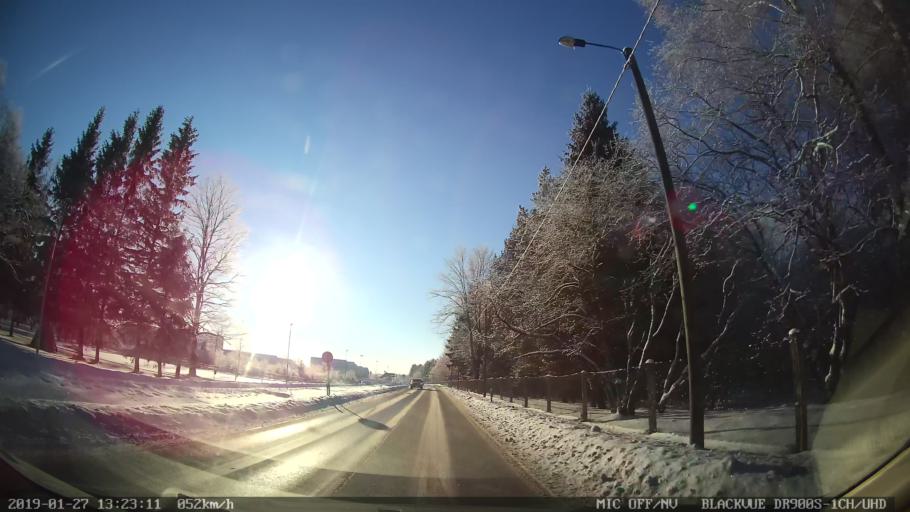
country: EE
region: Harju
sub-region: Tallinna linn
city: Tallinn
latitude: 59.4081
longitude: 24.7966
